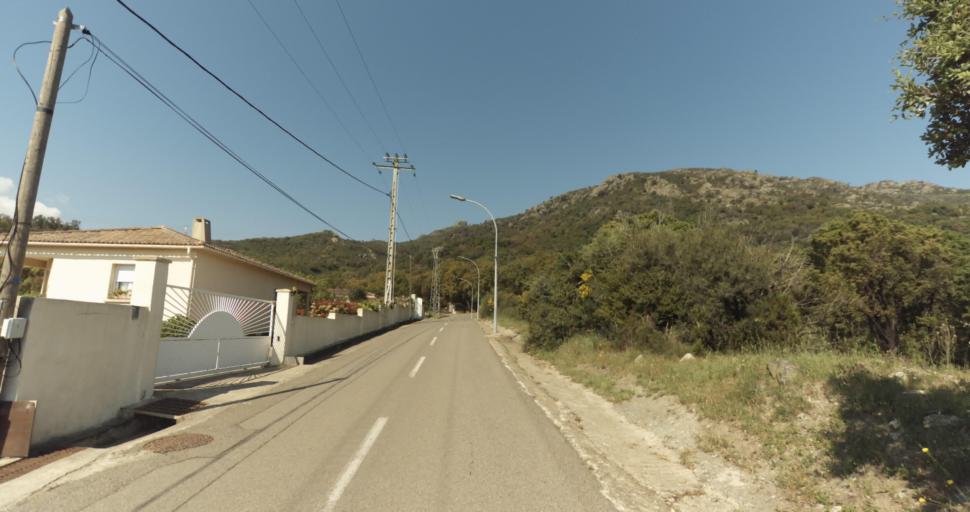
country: FR
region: Corsica
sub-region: Departement de la Haute-Corse
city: Biguglia
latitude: 42.6220
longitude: 9.4235
